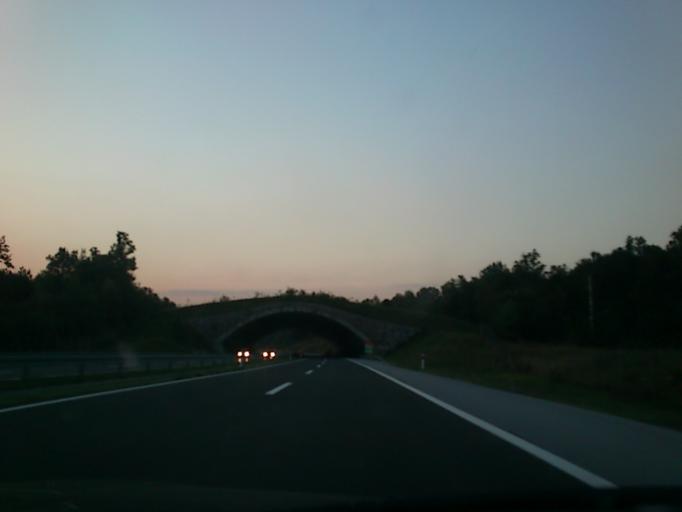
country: HR
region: Karlovacka
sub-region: Grad Ogulin
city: Ogulin
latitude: 45.3718
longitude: 15.2698
